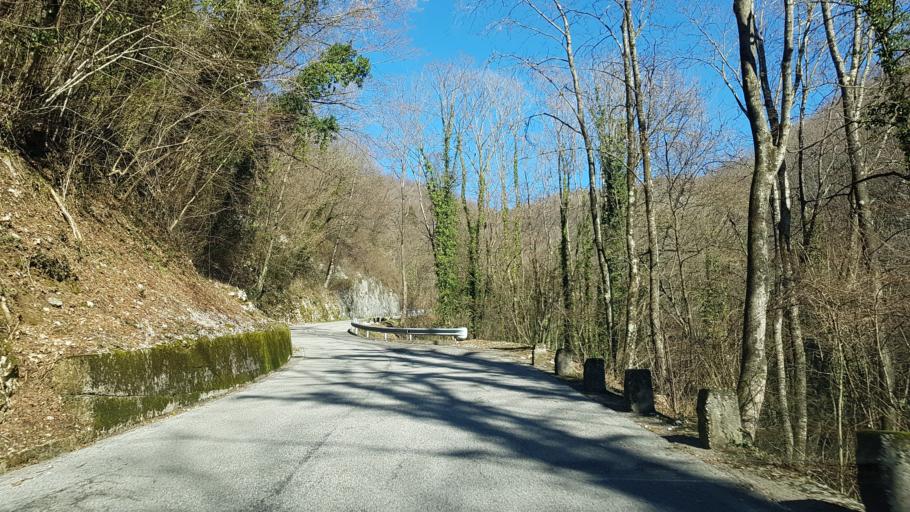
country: IT
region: Friuli Venezia Giulia
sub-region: Provincia di Udine
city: Attimis
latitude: 46.2306
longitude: 13.3037
